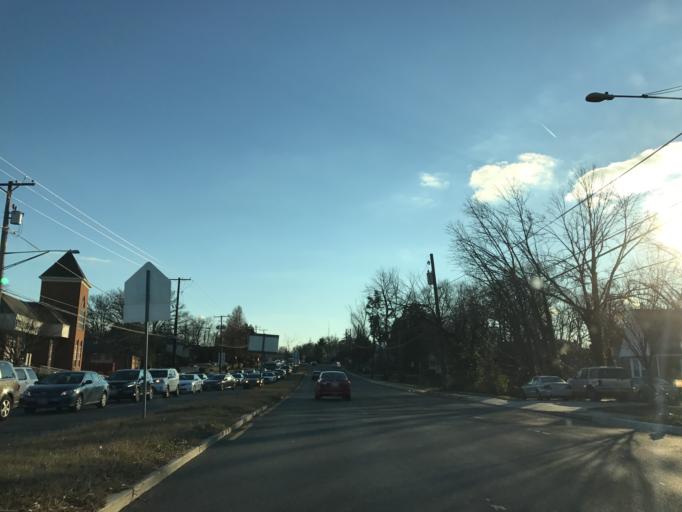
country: US
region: Maryland
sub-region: Montgomery County
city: Glenmont
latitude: 39.0525
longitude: -77.0511
